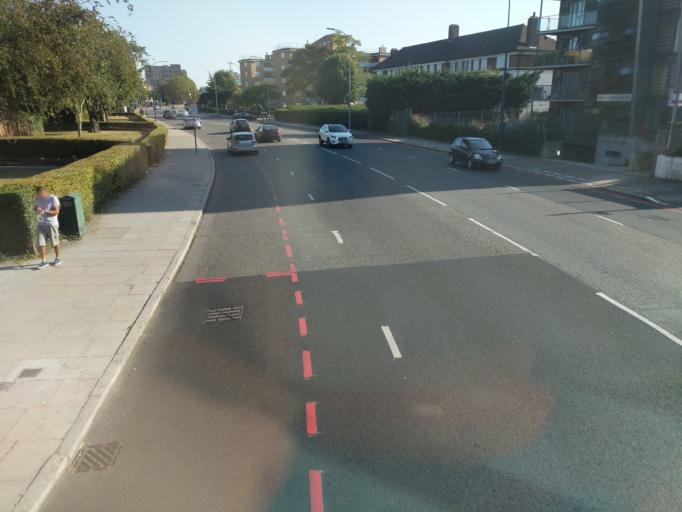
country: GB
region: England
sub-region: Greater London
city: Catford
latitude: 51.4326
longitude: -0.0172
